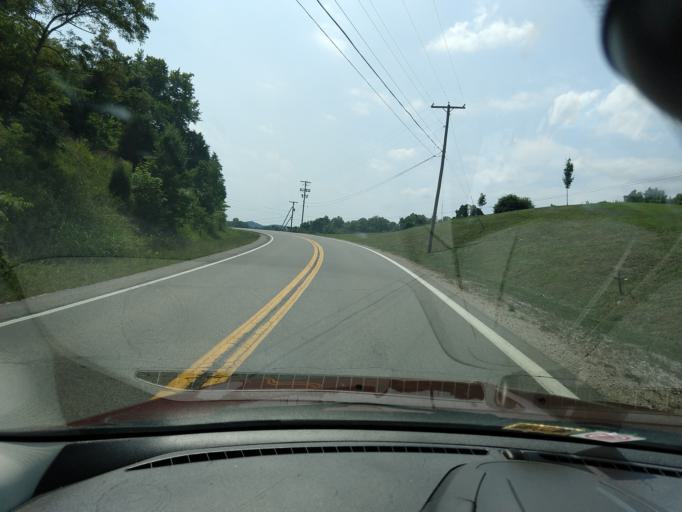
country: US
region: West Virginia
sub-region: Jackson County
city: Ravenswood
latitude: 38.8809
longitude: -81.8350
